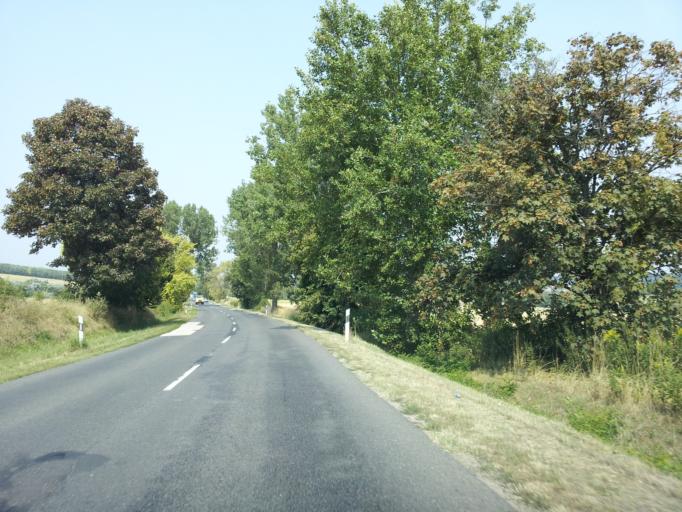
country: HU
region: Gyor-Moson-Sopron
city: Pannonhalma
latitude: 47.4933
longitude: 17.7798
